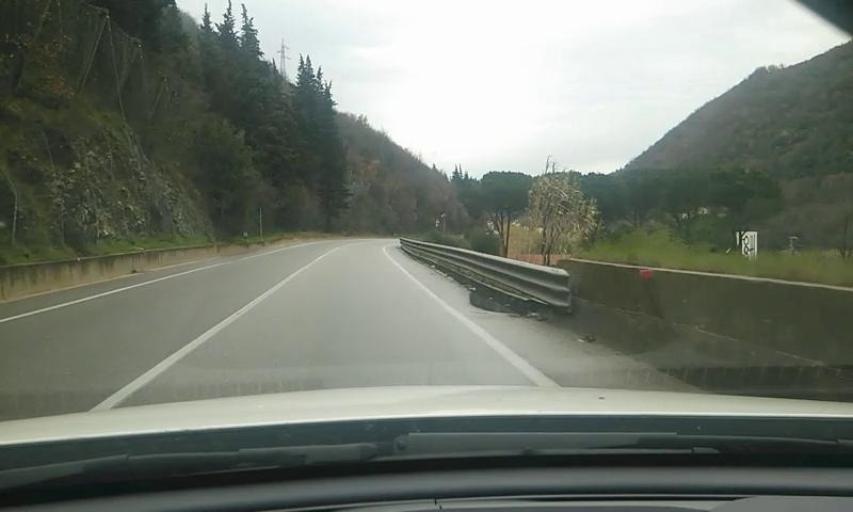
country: IT
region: Tuscany
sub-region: Provincia di Prato
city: Vaiano
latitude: 43.9162
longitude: 11.1254
